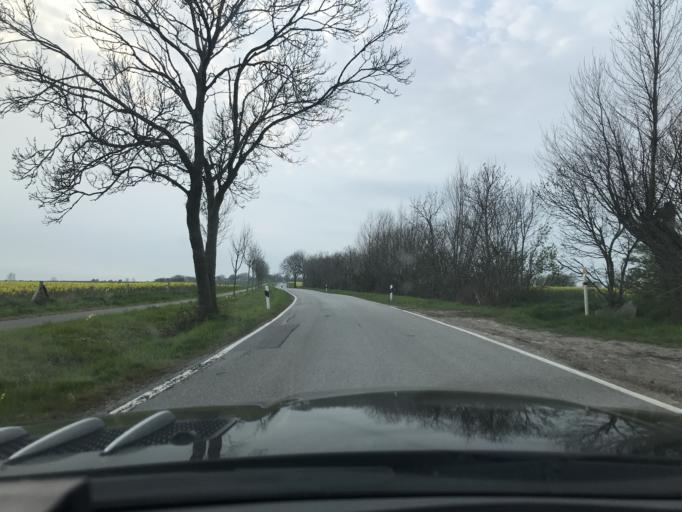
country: DE
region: Schleswig-Holstein
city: Burg auf Fehmarn
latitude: 54.4184
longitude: 11.2661
